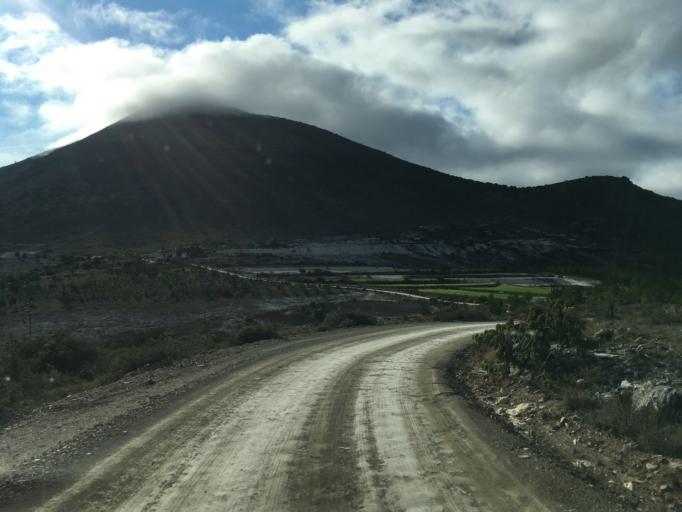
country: MX
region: Hidalgo
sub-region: Cardonal
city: Pozuelos
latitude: 20.6242
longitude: -98.9777
